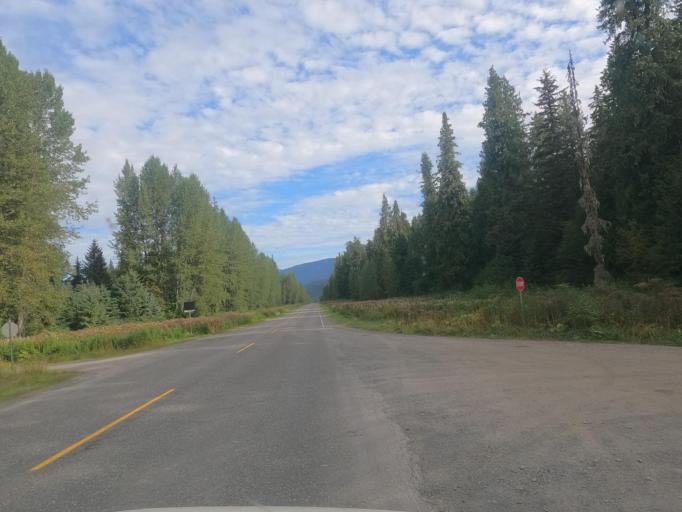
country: CA
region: British Columbia
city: Terrace
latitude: 55.3251
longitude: -128.0899
